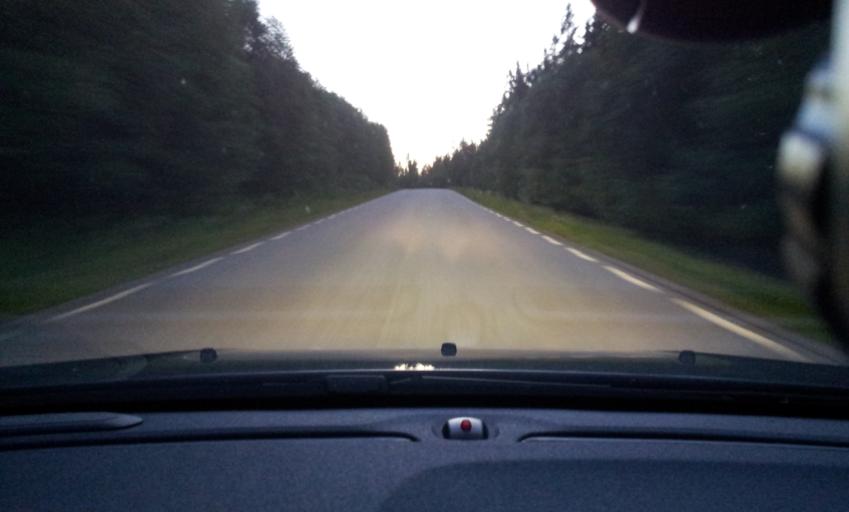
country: SE
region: Jaemtland
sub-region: Braecke Kommun
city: Braecke
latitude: 62.7274
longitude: 15.4086
